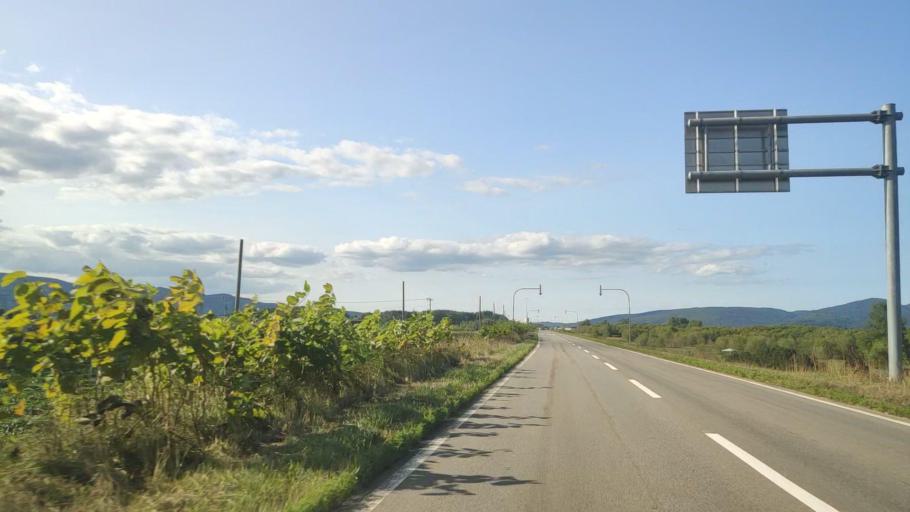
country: JP
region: Hokkaido
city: Nayoro
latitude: 44.8057
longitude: 142.0671
